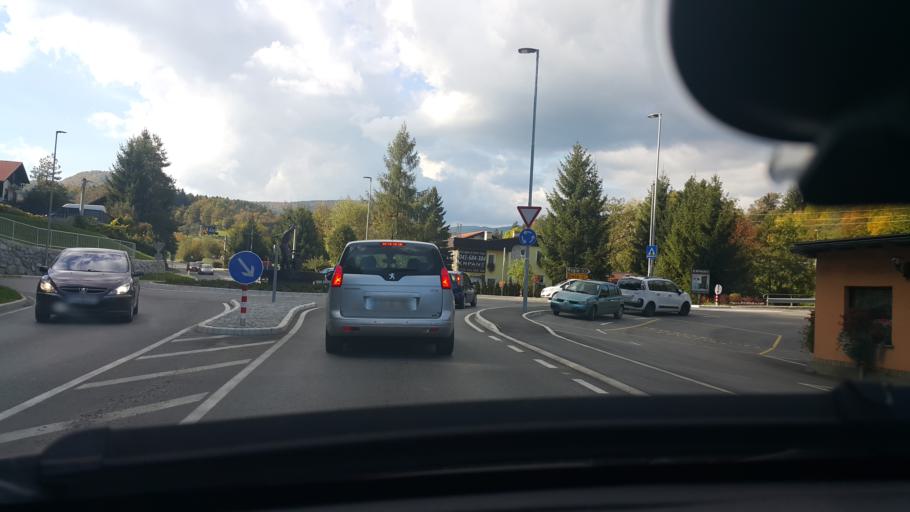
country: SI
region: Zrece
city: Zrece
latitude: 46.3593
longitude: 15.3954
